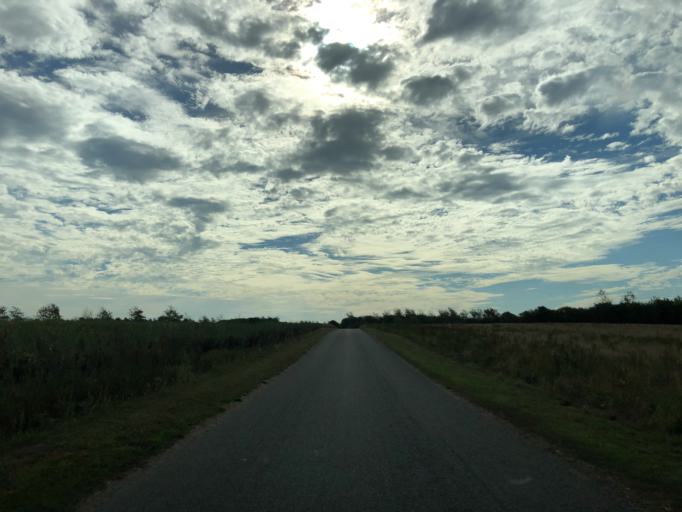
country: DK
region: Central Jutland
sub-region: Ringkobing-Skjern Kommune
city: Skjern
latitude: 56.0426
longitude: 8.4332
